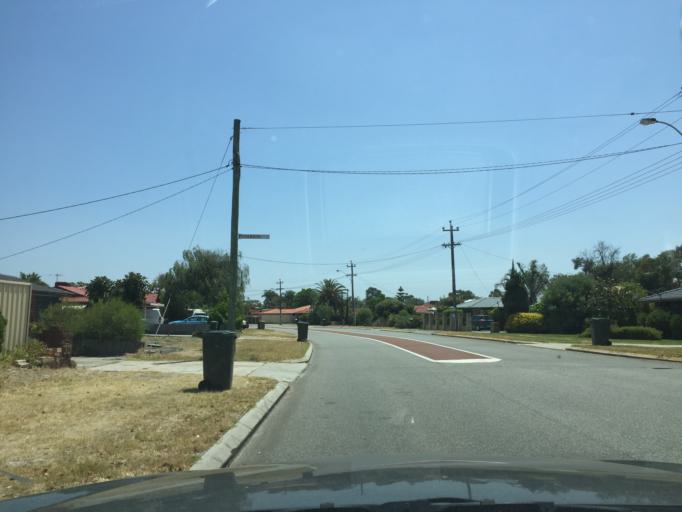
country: AU
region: Western Australia
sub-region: Canning
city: Ferndale
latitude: -32.0414
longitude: 115.9133
